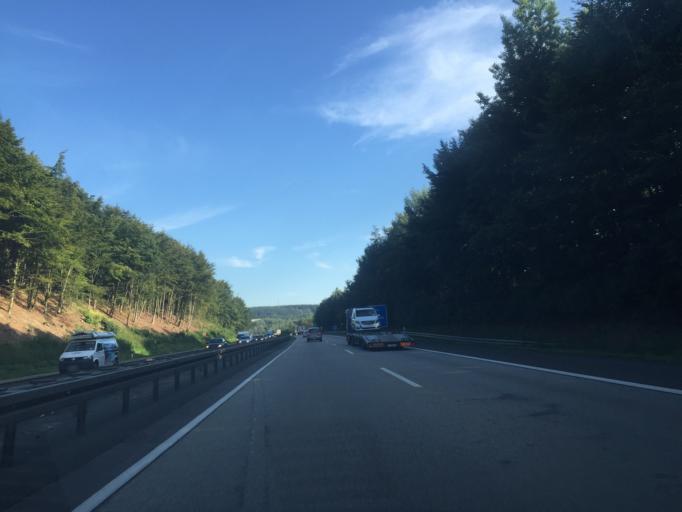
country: DE
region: North Rhine-Westphalia
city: Freudenberg
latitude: 50.9023
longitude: 7.9182
